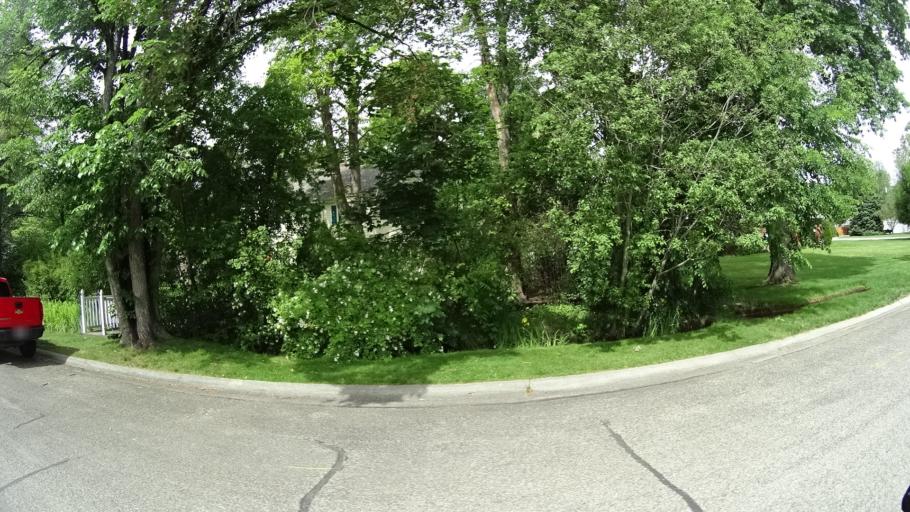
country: US
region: Idaho
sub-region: Ada County
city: Boise
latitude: 43.5902
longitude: -116.1999
